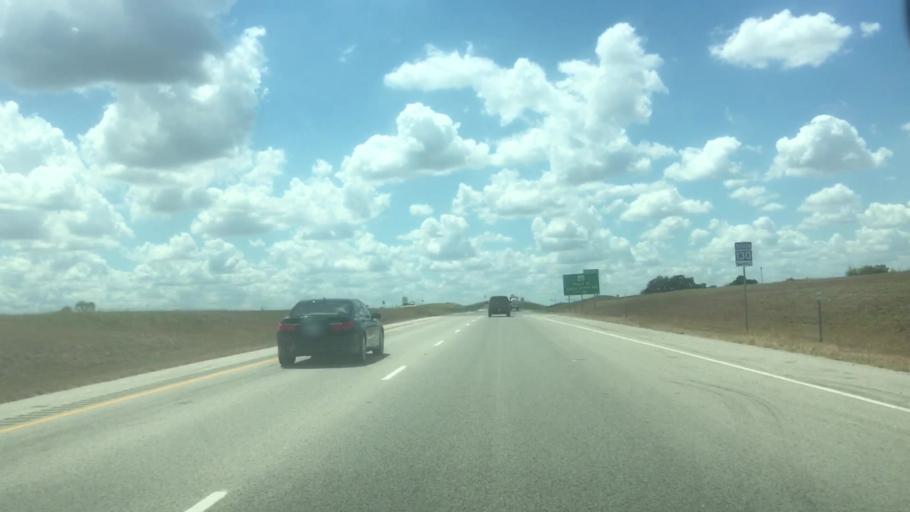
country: US
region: Texas
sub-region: Caldwell County
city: Lockhart
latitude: 29.9054
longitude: -97.6955
